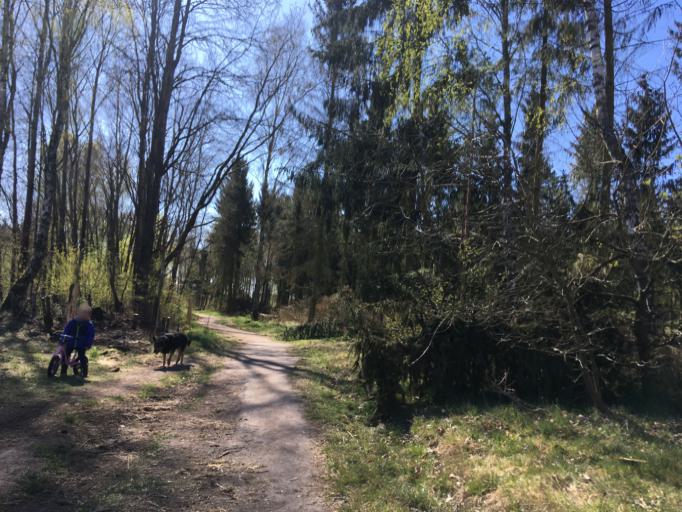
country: DE
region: Brandenburg
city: Wandlitz
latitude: 52.6868
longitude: 13.4648
